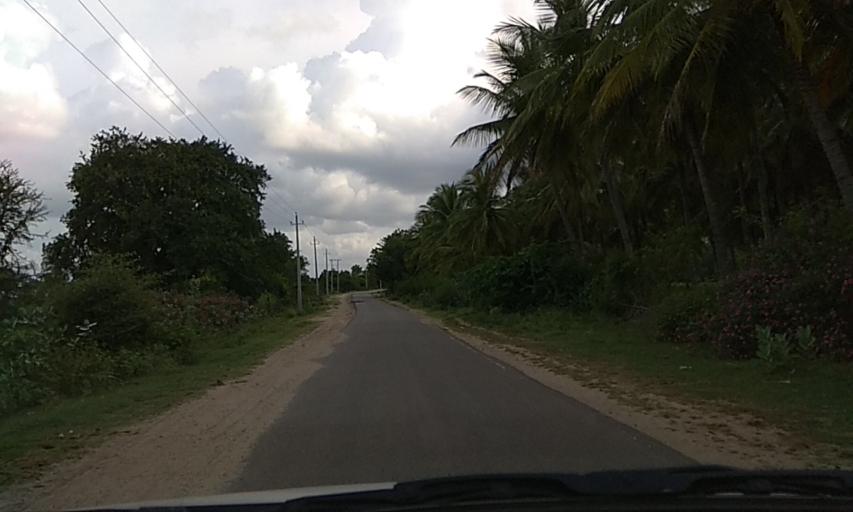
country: IN
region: Karnataka
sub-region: Chamrajnagar
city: Gundlupet
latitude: 11.8811
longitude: 76.7473
